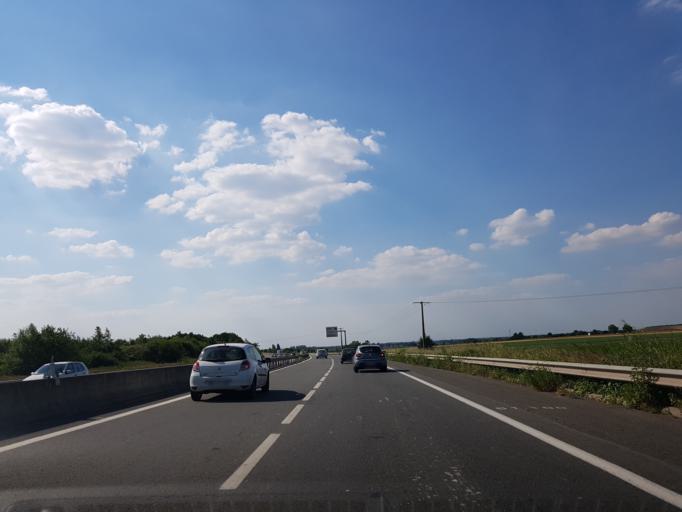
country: FR
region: Nord-Pas-de-Calais
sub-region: Departement du Nord
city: Abscon
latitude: 50.3396
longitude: 3.3178
